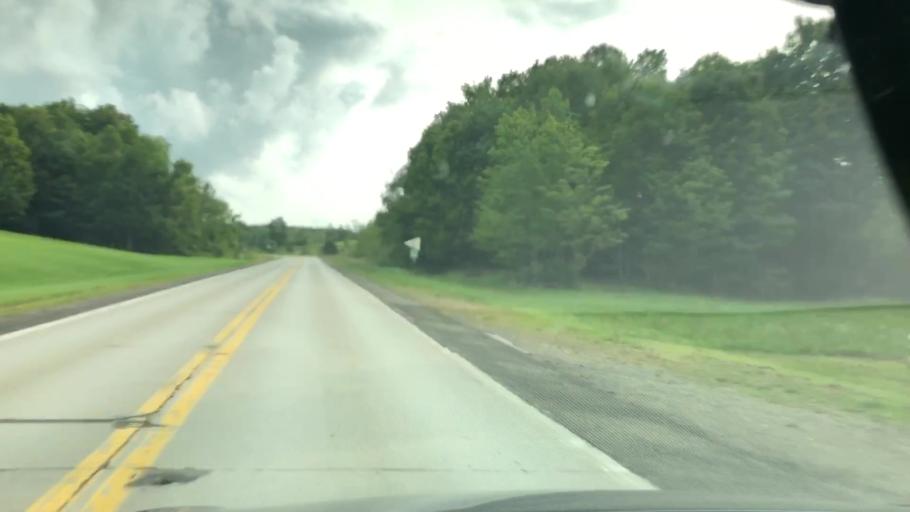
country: US
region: Pennsylvania
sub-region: Erie County
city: Union City
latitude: 41.9640
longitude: -79.8517
